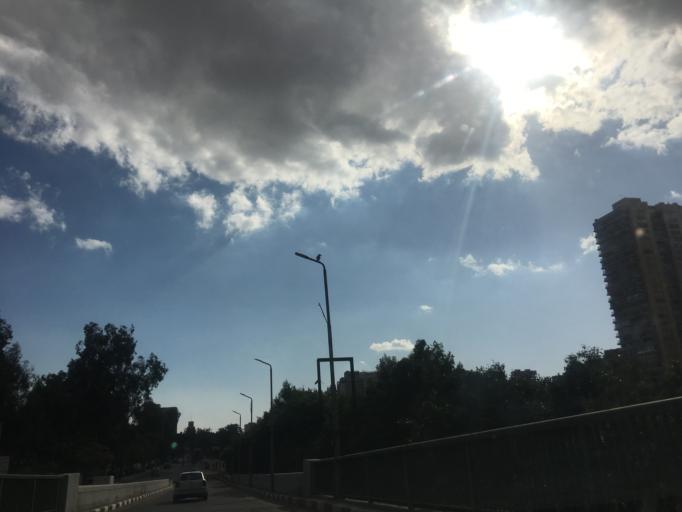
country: EG
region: Muhafazat al Qahirah
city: Cairo
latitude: 30.0474
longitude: 31.2196
